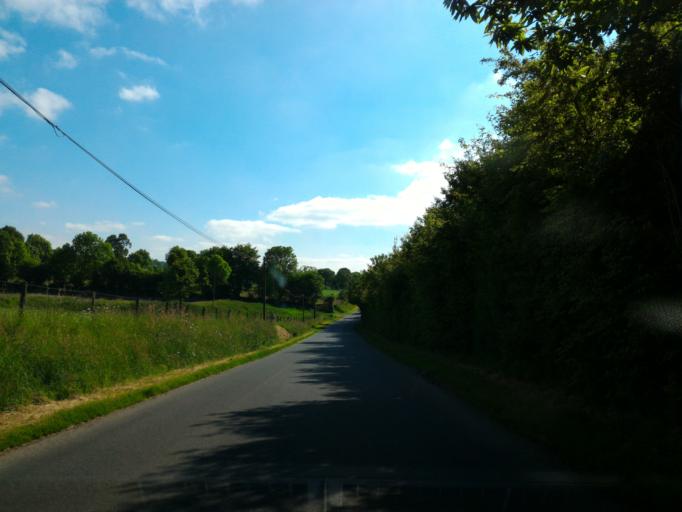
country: FR
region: Lower Normandy
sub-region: Departement de la Manche
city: Percy
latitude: 48.8729
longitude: -1.1857
